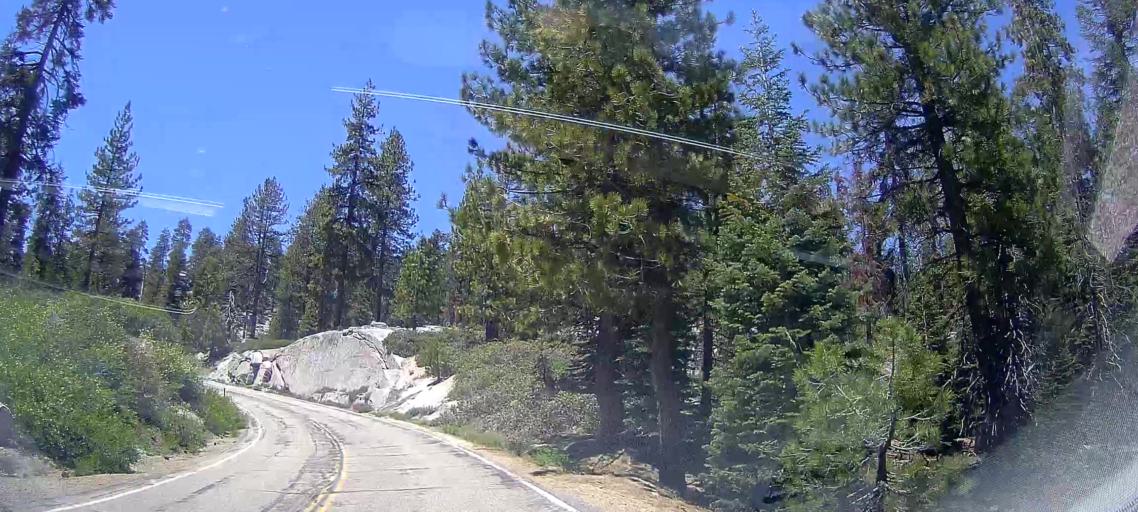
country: US
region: California
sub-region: Tulare County
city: Three Rivers
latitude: 36.7012
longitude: -118.8684
